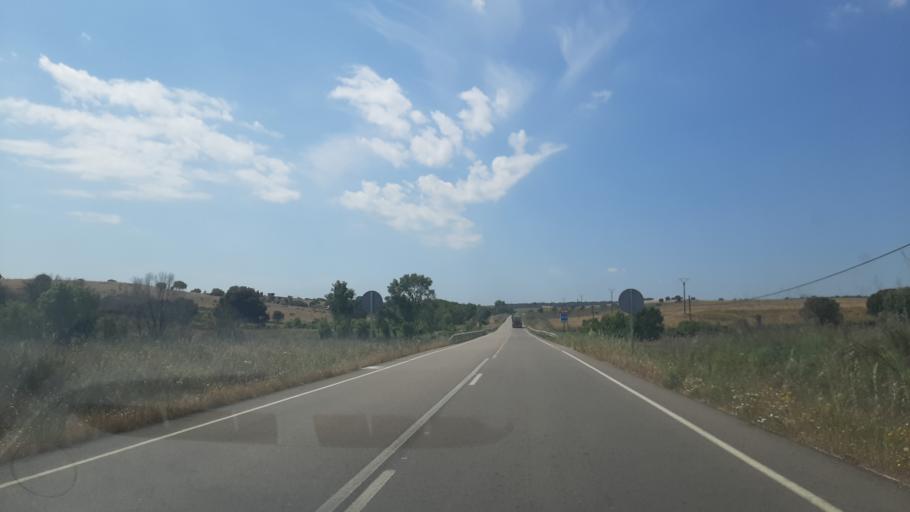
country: ES
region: Castille and Leon
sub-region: Provincia de Salamanca
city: Gallegos de Arganan
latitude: 40.6199
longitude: -6.7057
